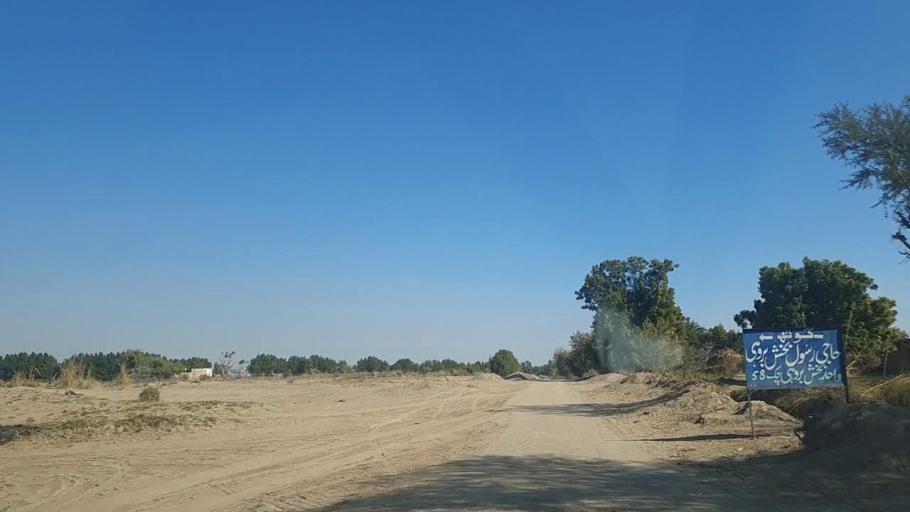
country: PK
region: Sindh
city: Sanghar
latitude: 26.2091
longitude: 68.9064
